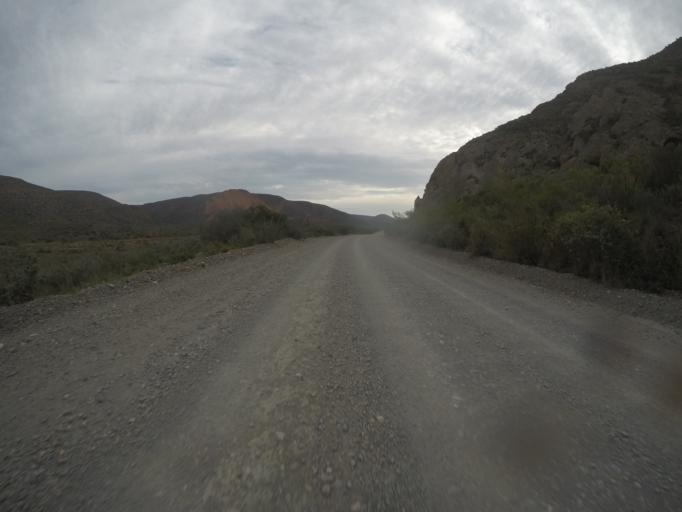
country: ZA
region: Eastern Cape
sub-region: Cacadu District Municipality
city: Willowmore
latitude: -33.5225
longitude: 23.6586
